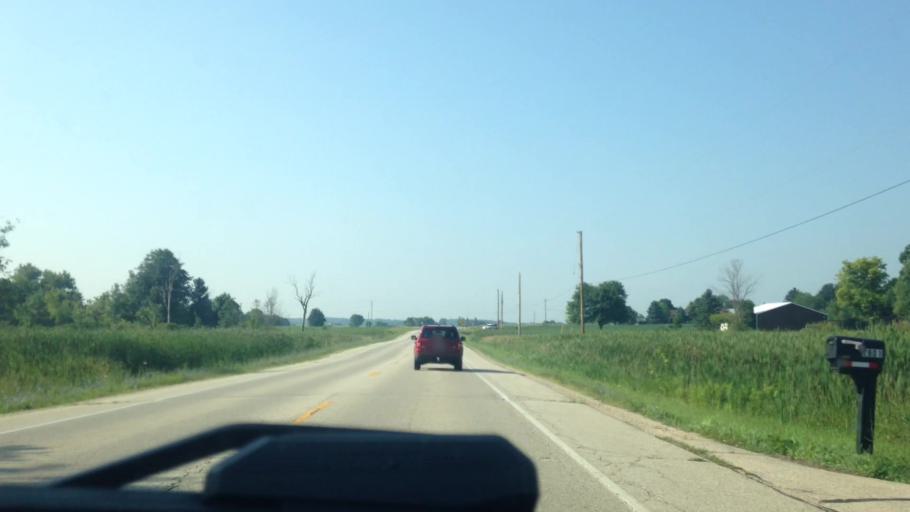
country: US
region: Wisconsin
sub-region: Washington County
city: Slinger
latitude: 43.2854
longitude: -88.2610
